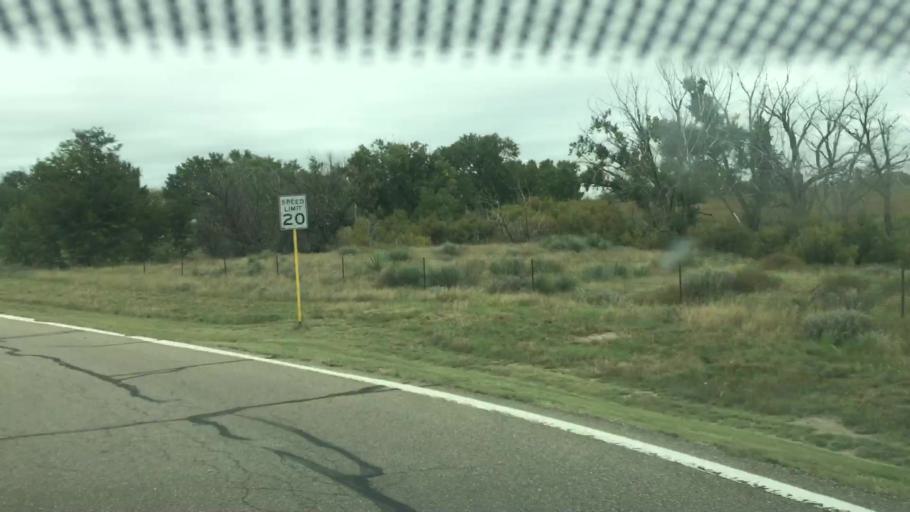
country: US
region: Kansas
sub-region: Hamilton County
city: Syracuse
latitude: 38.0502
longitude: -102.0538
